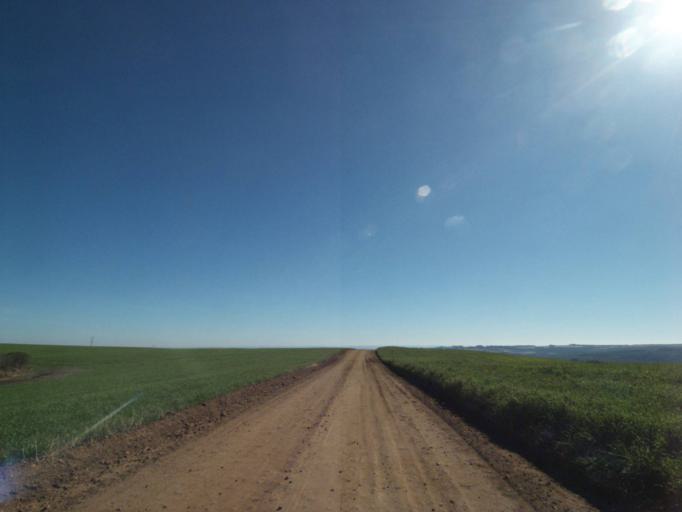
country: BR
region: Parana
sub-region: Tibagi
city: Tibagi
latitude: -24.5746
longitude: -50.2656
